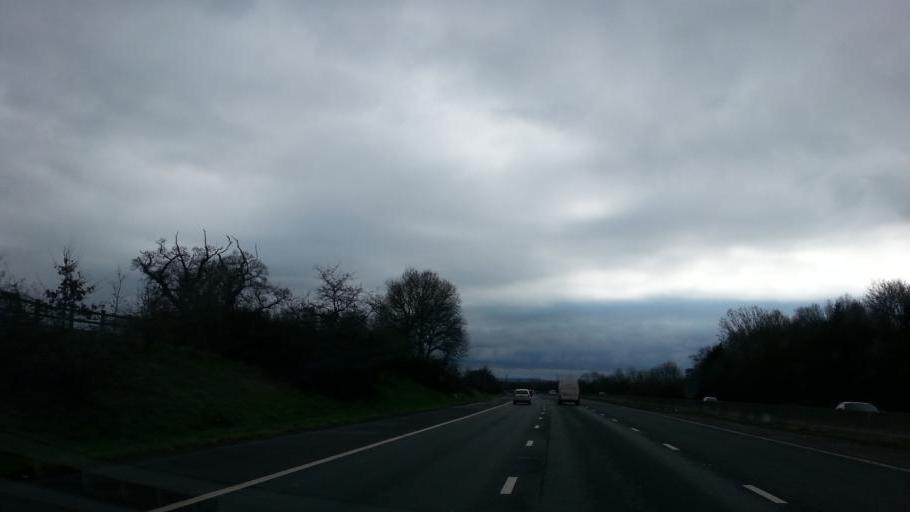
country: GB
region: England
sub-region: Somerset
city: North Petherton
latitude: 51.0929
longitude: -3.0023
